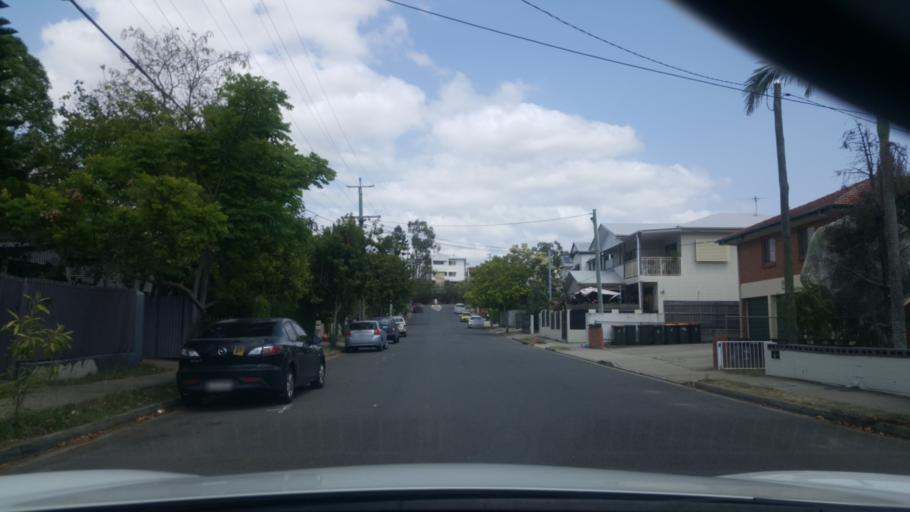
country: AU
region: Queensland
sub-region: Brisbane
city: South Brisbane
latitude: -27.4842
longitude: 153.0214
